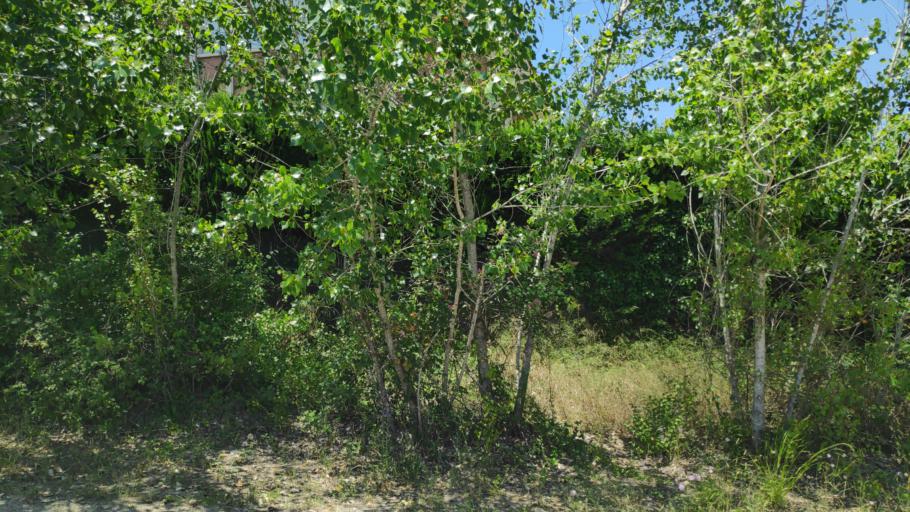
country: ES
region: Catalonia
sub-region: Provincia de Barcelona
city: Sant Quirze del Valles
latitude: 41.5112
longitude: 2.0928
